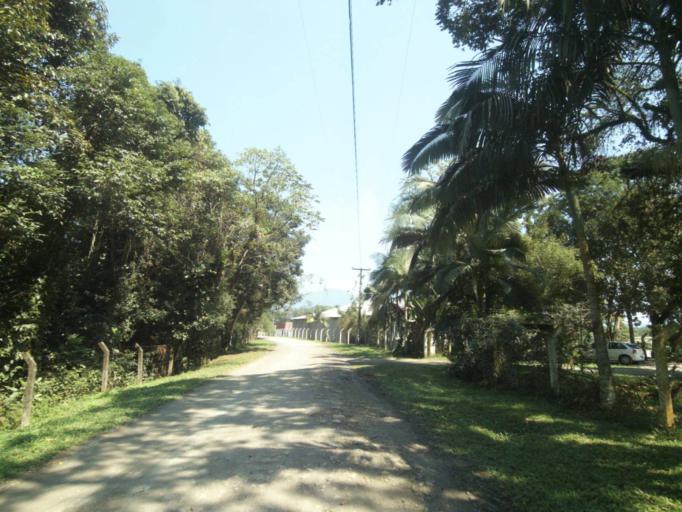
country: BR
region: Parana
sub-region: Paranagua
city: Paranagua
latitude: -25.5493
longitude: -48.5903
